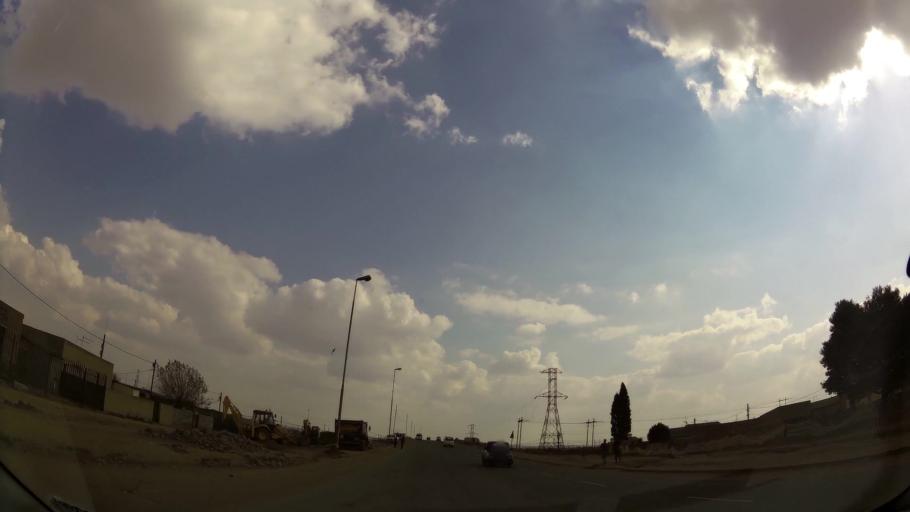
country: ZA
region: Gauteng
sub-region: Ekurhuleni Metropolitan Municipality
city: Springs
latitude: -26.1180
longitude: 28.4709
